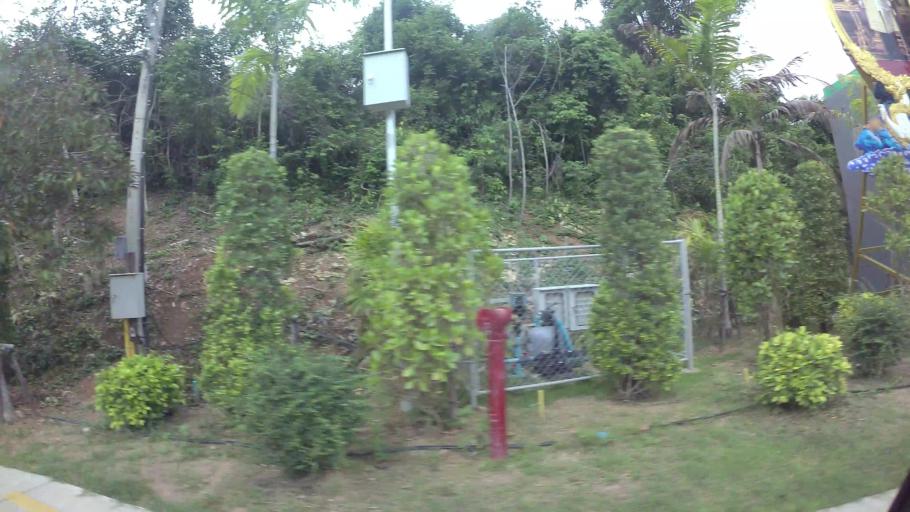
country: TH
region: Chon Buri
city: Si Racha
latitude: 13.2077
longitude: 100.9611
